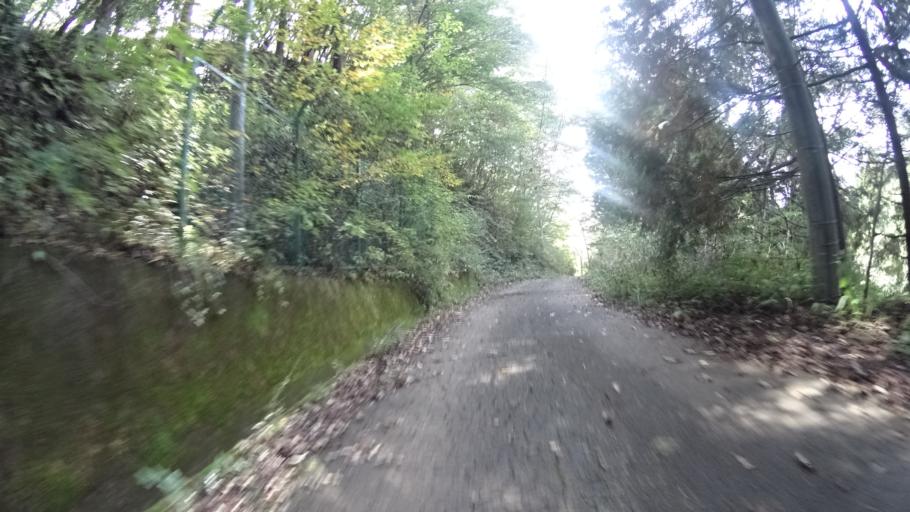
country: JP
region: Yamanashi
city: Otsuki
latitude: 35.5735
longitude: 138.9906
